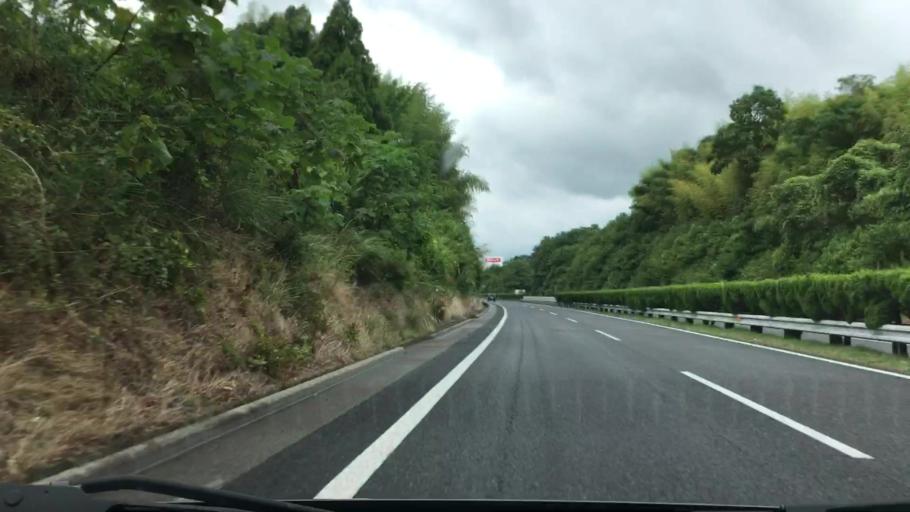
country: JP
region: Okayama
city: Tsuyama
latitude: 35.0445
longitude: 134.1131
